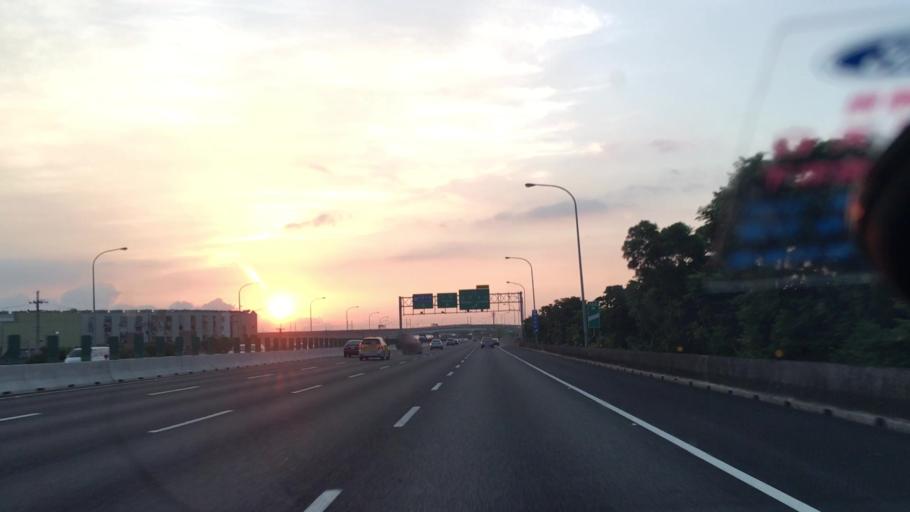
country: TW
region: Taiwan
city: Taoyuan City
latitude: 25.0317
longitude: 121.2451
